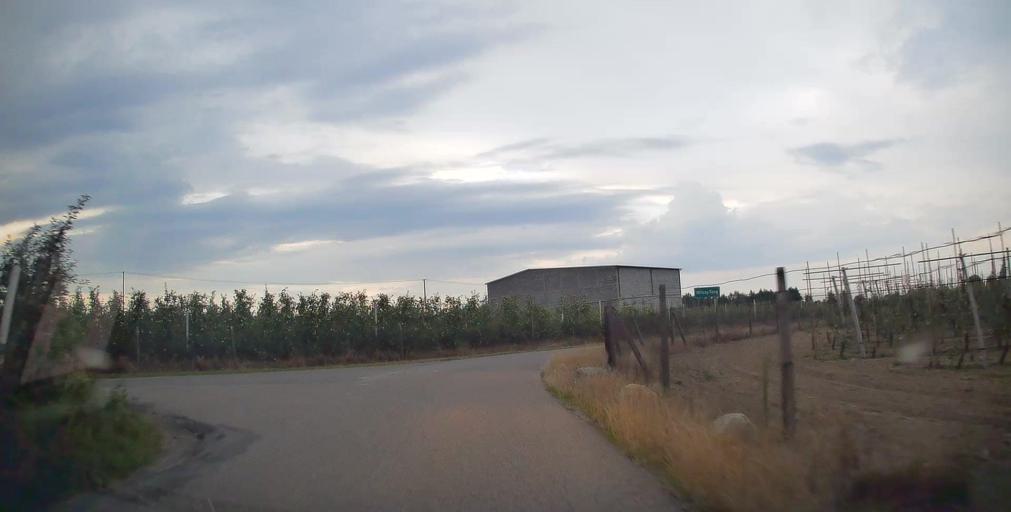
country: PL
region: Masovian Voivodeship
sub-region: Powiat grojecki
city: Jasieniec
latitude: 51.7906
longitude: 20.8982
